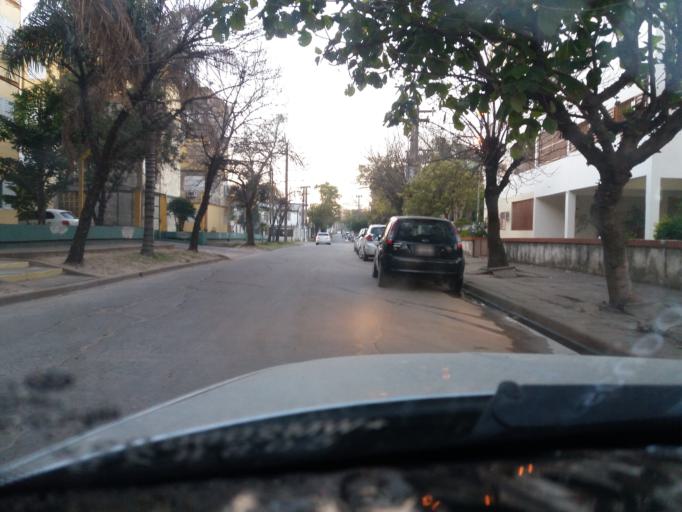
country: AR
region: Corrientes
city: Corrientes
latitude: -27.4854
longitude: -58.8443
